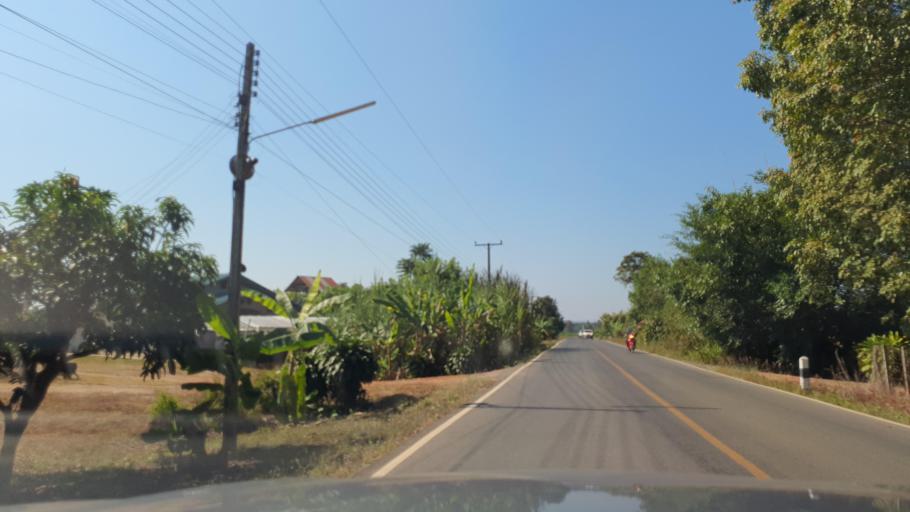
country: TH
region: Nan
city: Pua
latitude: 19.1321
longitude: 100.9287
